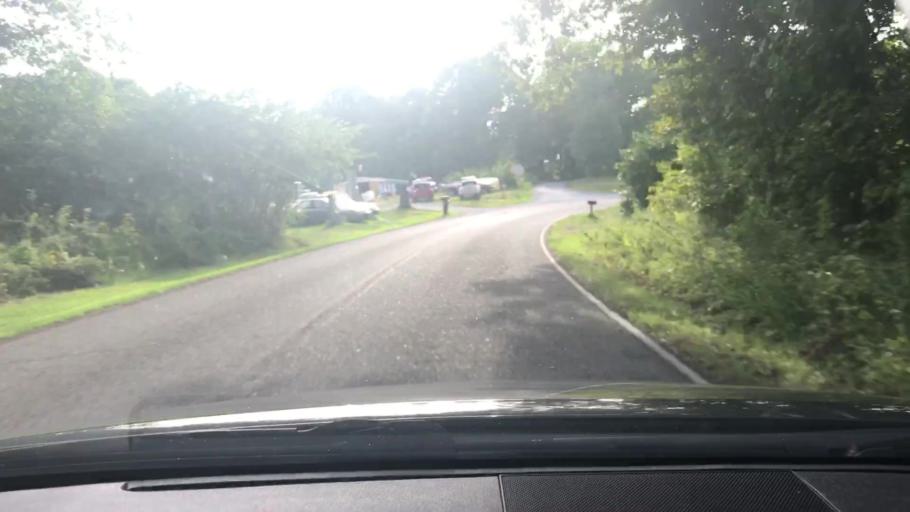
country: US
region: Tennessee
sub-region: Dickson County
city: White Bluff
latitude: 36.1577
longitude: -87.2525
